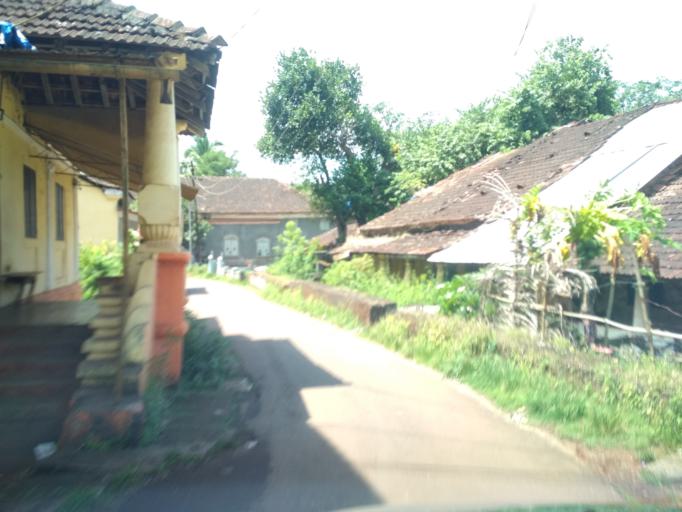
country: IN
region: Goa
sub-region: North Goa
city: Serula
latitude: 15.5483
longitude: 73.8211
